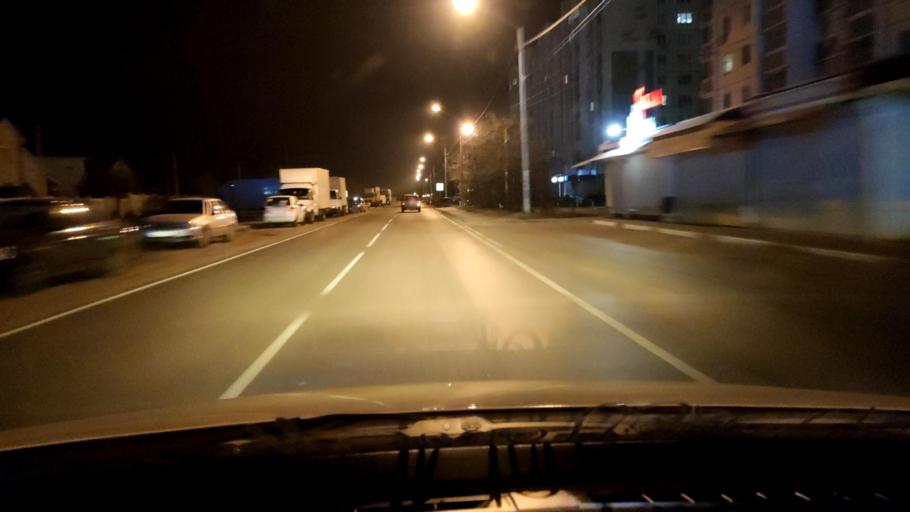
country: RU
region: Voronezj
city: Pridonskoy
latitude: 51.6204
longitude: 39.0653
